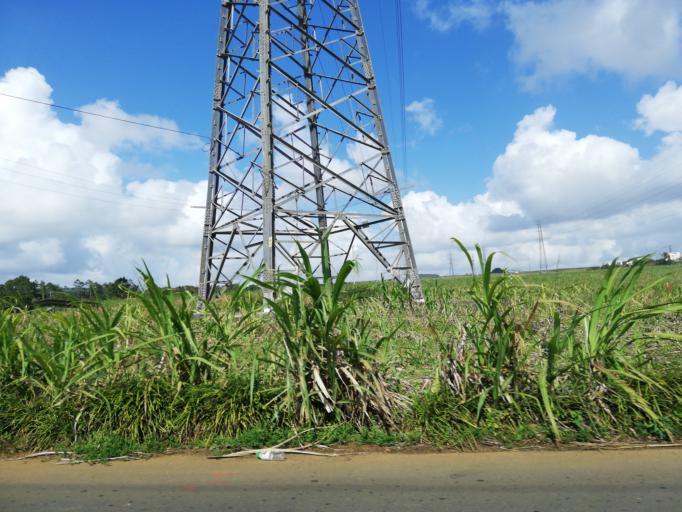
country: MU
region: Moka
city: Verdun
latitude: -20.2139
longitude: 57.5539
